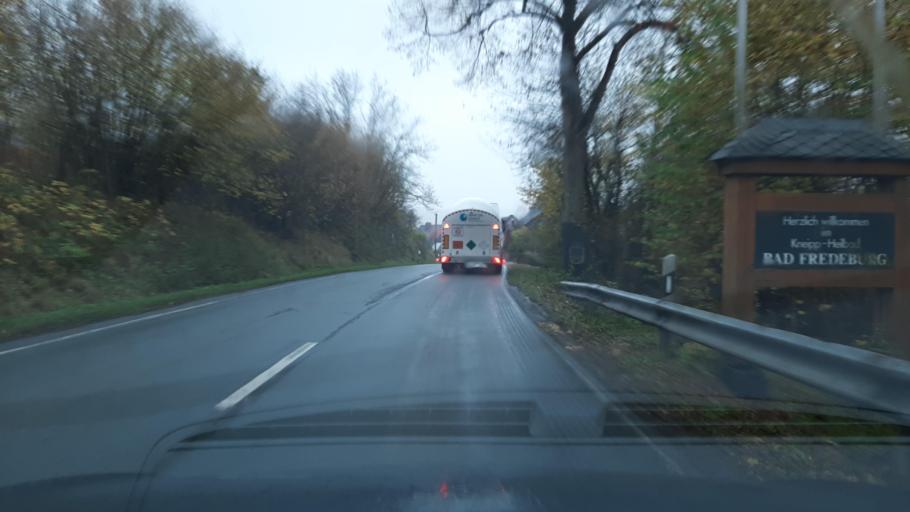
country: DE
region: North Rhine-Westphalia
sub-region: Regierungsbezirk Arnsberg
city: Bad Fredeburg
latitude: 51.1959
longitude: 8.3096
